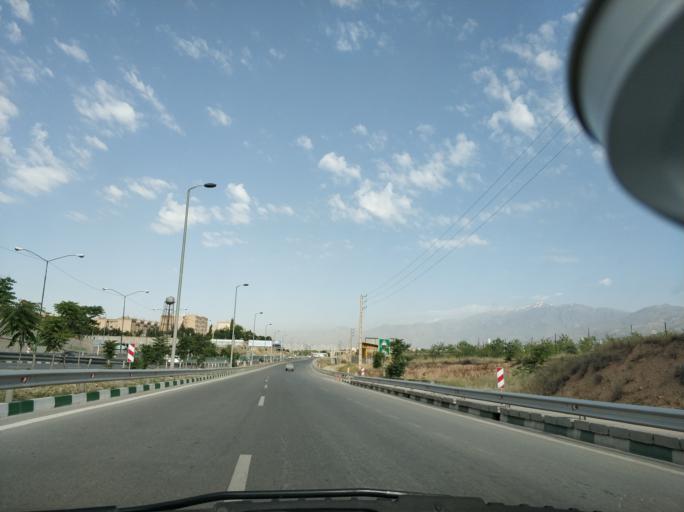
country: IR
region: Tehran
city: Tajrish
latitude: 35.7456
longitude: 51.6024
